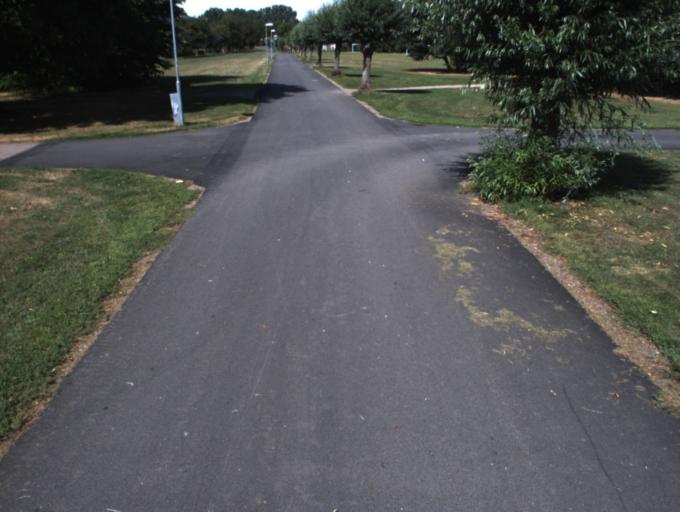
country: SE
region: Skane
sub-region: Helsingborg
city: Helsingborg
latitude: 56.0581
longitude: 12.7255
